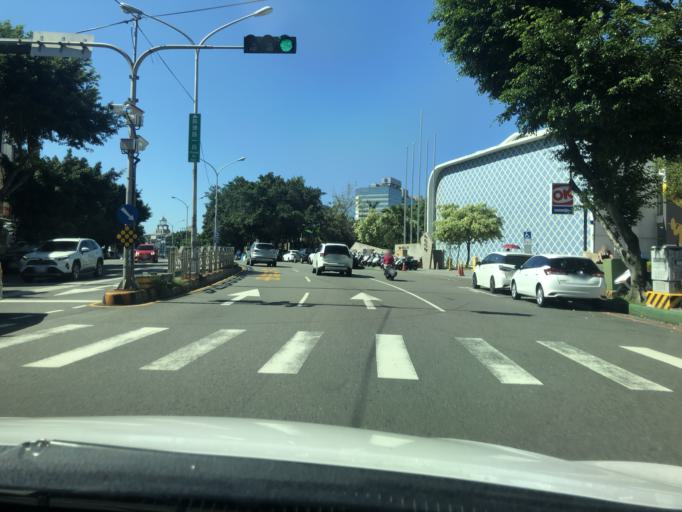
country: TW
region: Taiwan
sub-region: Taichung City
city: Taichung
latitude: 24.1576
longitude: 120.6850
